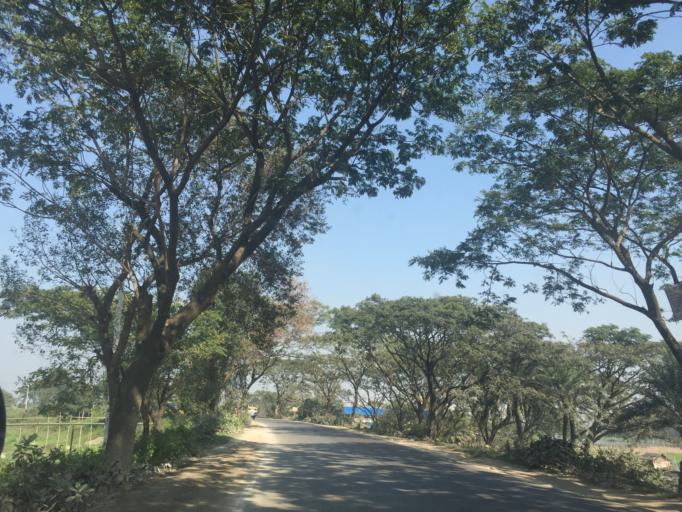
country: BD
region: Dhaka
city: Tungi
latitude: 23.8407
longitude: 90.3427
